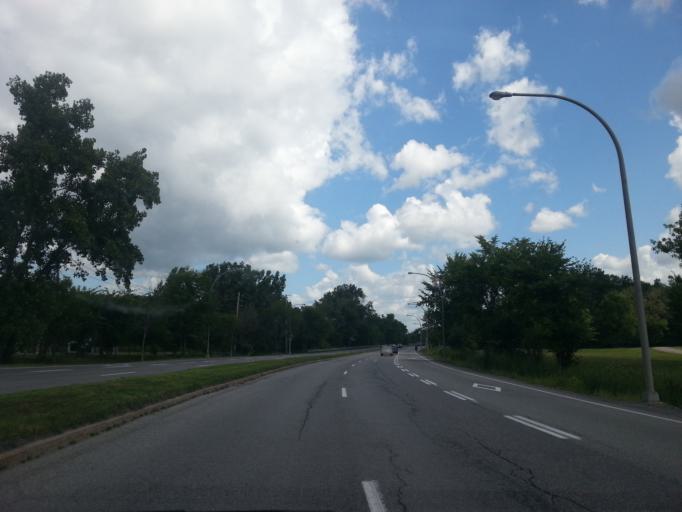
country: CA
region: Quebec
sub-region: Outaouais
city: Gatineau
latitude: 45.4490
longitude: -75.7115
